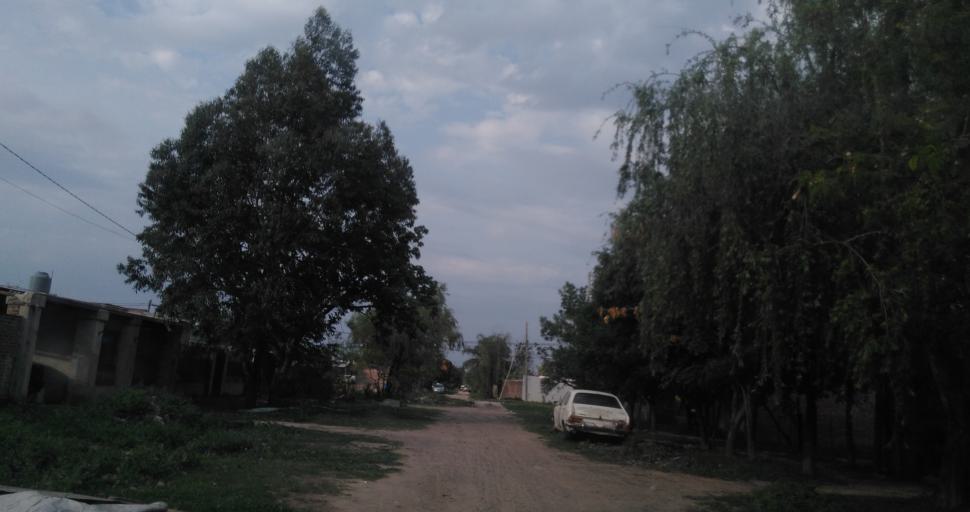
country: AR
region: Chaco
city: Resistencia
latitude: -27.4822
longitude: -59.0007
